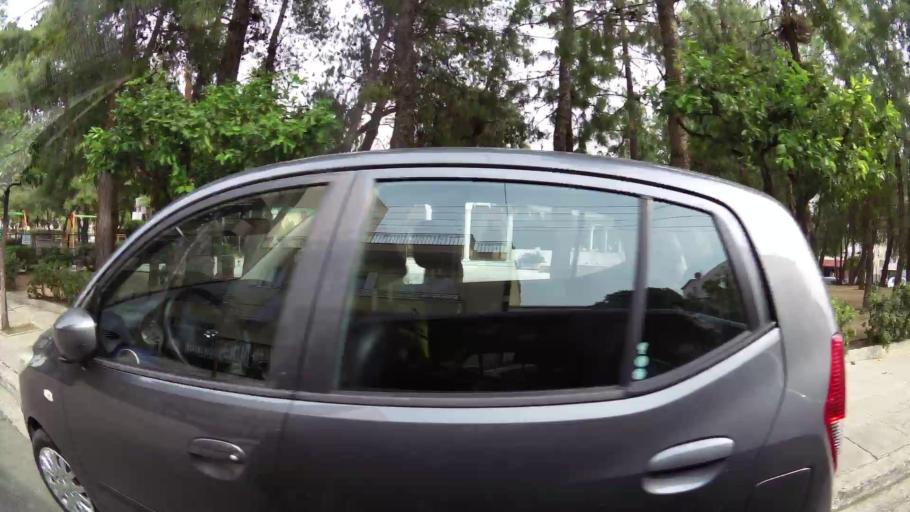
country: GR
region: Attica
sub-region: Nomarchia Athinas
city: Nea Ionia
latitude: 38.0341
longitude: 23.7667
